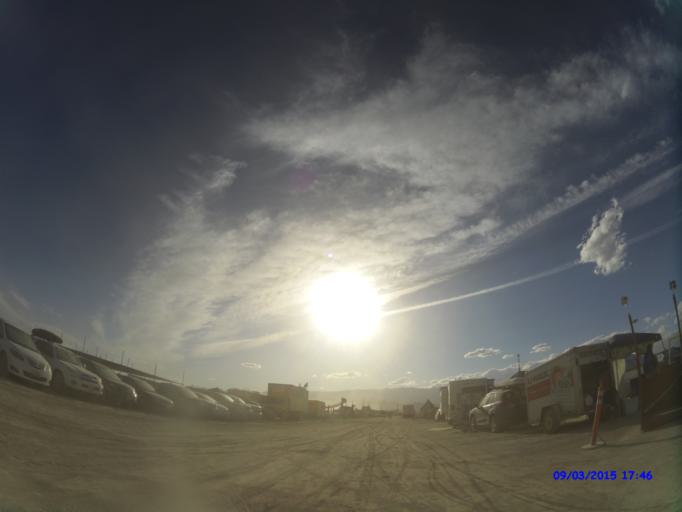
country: US
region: Nevada
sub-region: Pershing County
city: Lovelock
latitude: 40.7750
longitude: -119.2066
